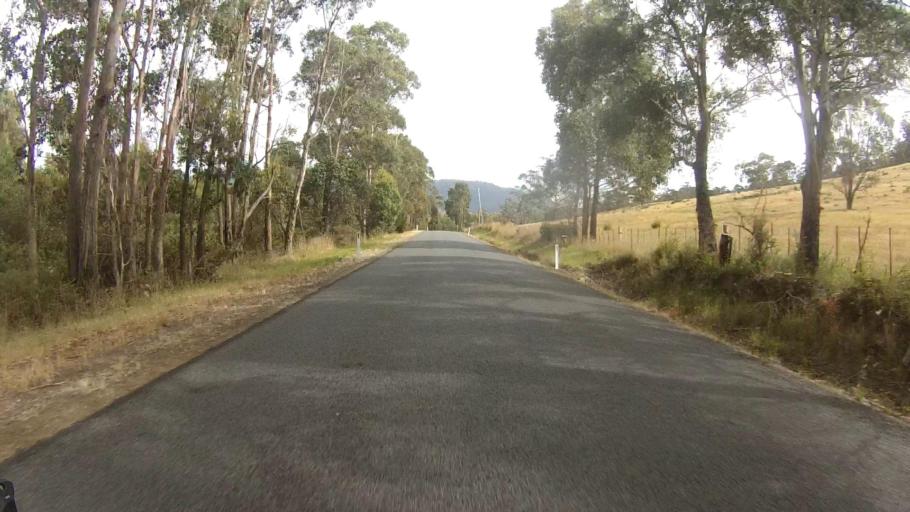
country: AU
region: Tasmania
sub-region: Sorell
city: Sorell
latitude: -42.8066
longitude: 147.7941
